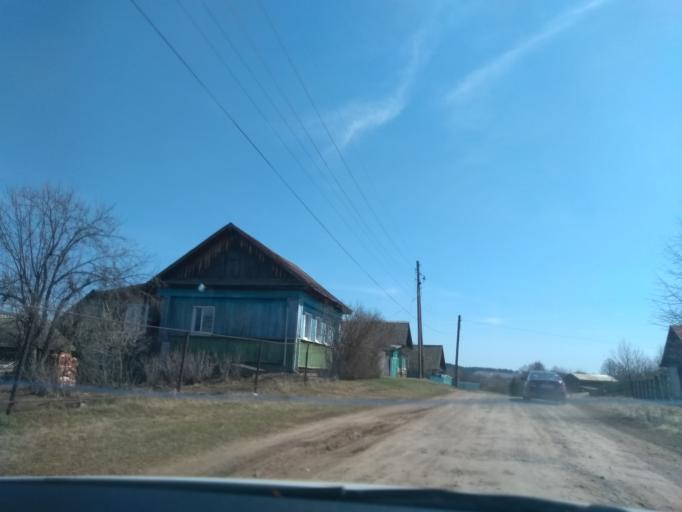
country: RU
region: Perm
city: Uinskoye
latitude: 57.1777
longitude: 56.5714
